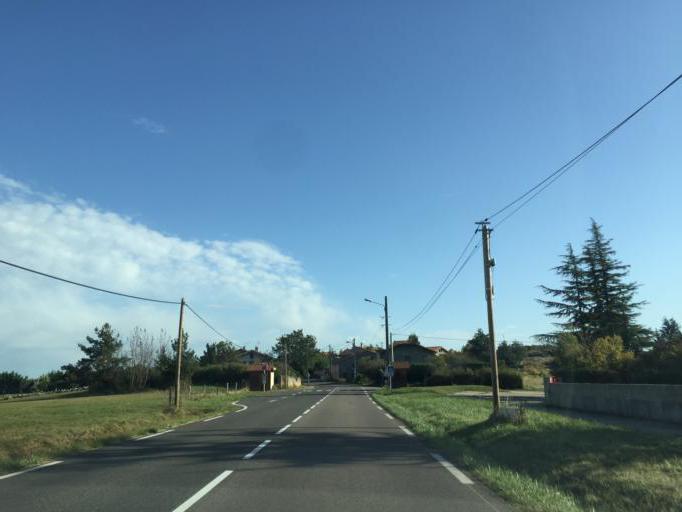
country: FR
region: Rhone-Alpes
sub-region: Departement de la Loire
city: Perigneux
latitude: 45.4606
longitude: 4.1149
